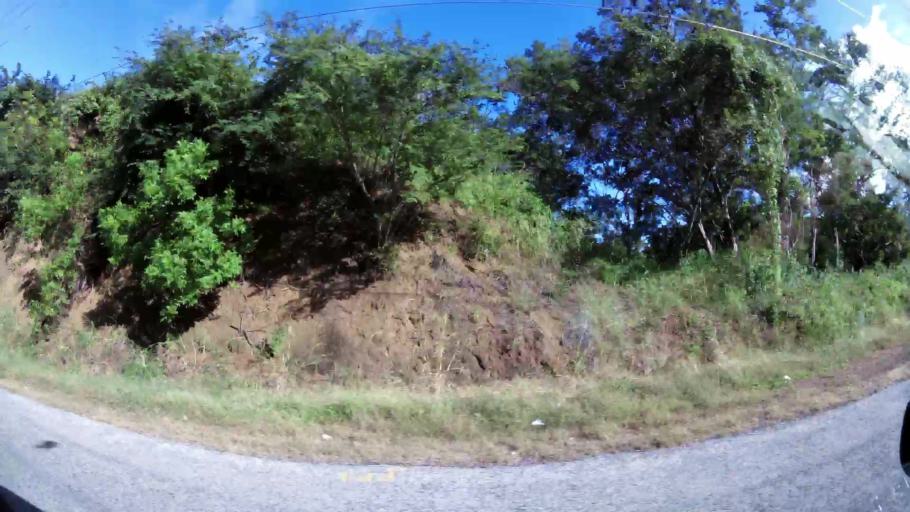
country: CR
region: Guanacaste
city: Sardinal
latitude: 10.5845
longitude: -85.6605
